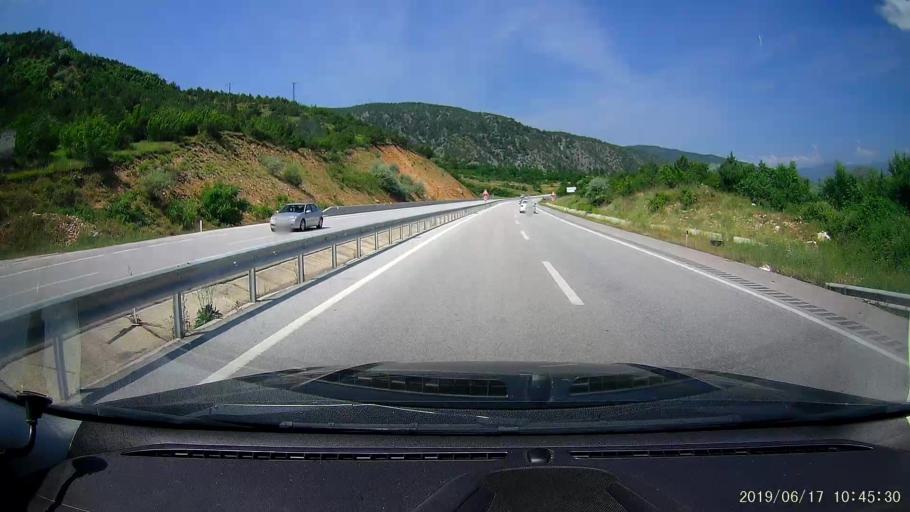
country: TR
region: Corum
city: Hacihamza
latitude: 41.0629
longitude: 34.4859
